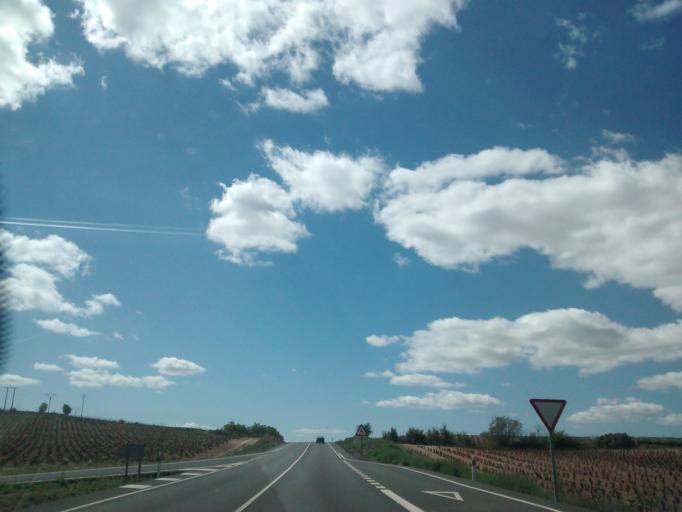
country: ES
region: La Rioja
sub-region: Provincia de La Rioja
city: Torremontalbo
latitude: 42.5070
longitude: -2.6973
